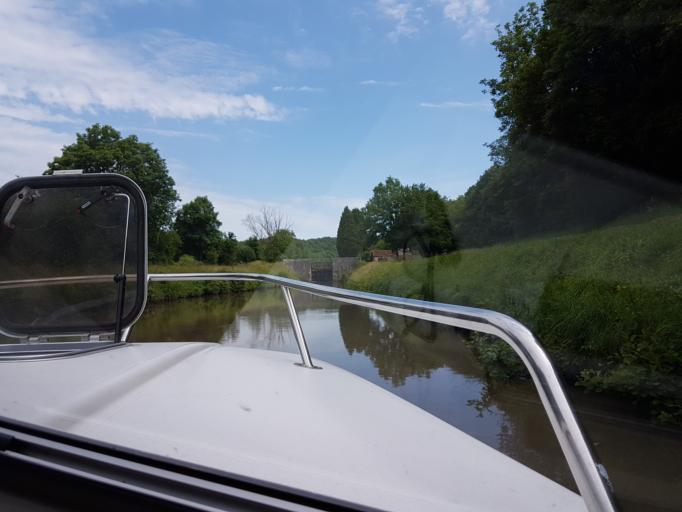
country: FR
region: Bourgogne
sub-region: Departement de la Nievre
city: Clamecy
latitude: 47.4520
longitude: 3.5380
